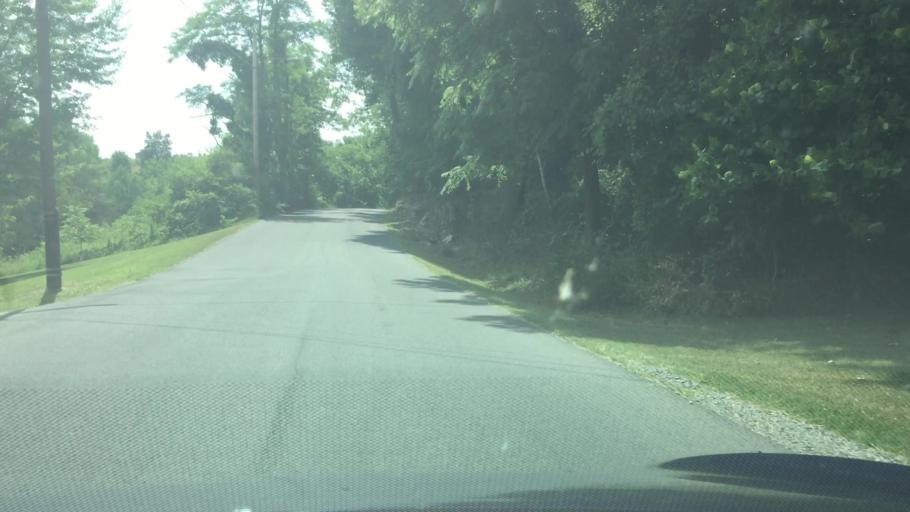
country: US
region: Virginia
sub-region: Wythe County
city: Wytheville
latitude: 36.9386
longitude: -81.0750
